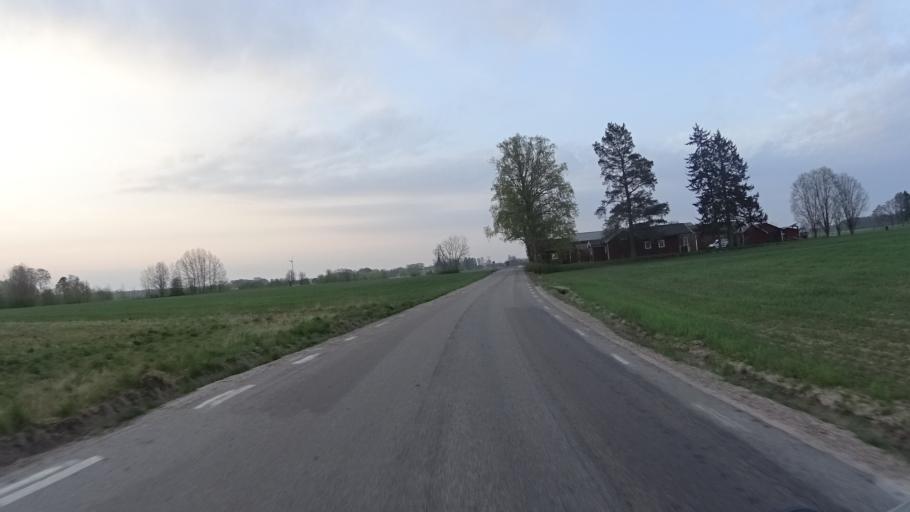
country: SE
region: Vaestra Goetaland
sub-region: Gotene Kommun
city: Kallby
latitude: 58.4804
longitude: 13.3186
